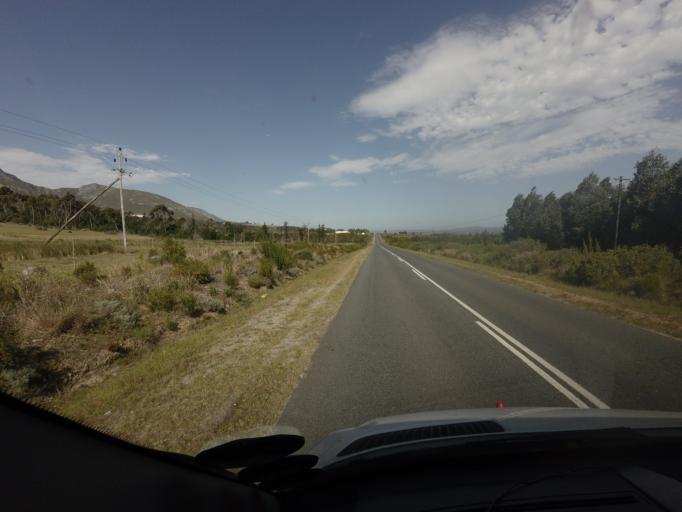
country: ZA
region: Western Cape
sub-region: Overberg District Municipality
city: Caledon
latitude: -34.4177
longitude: 19.4232
